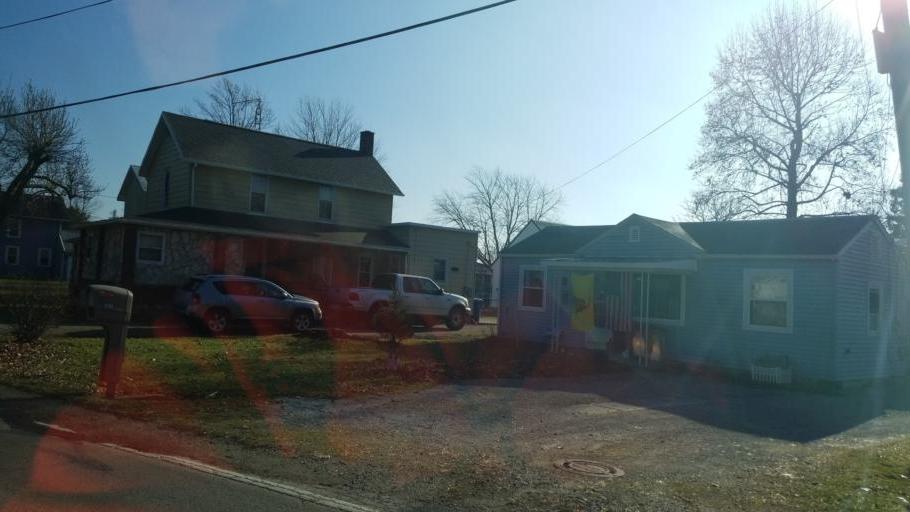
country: US
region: Ohio
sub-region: Seneca County
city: Tiffin
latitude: 41.1190
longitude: -83.1598
